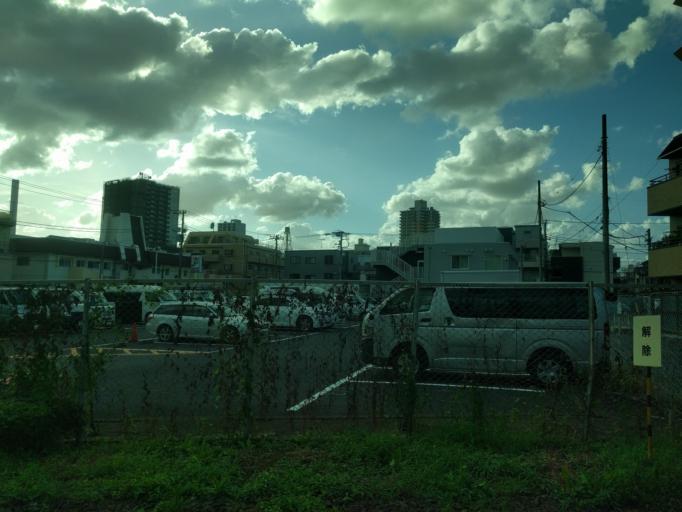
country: JP
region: Tokyo
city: Tokyo
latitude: 35.7365
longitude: 139.7274
